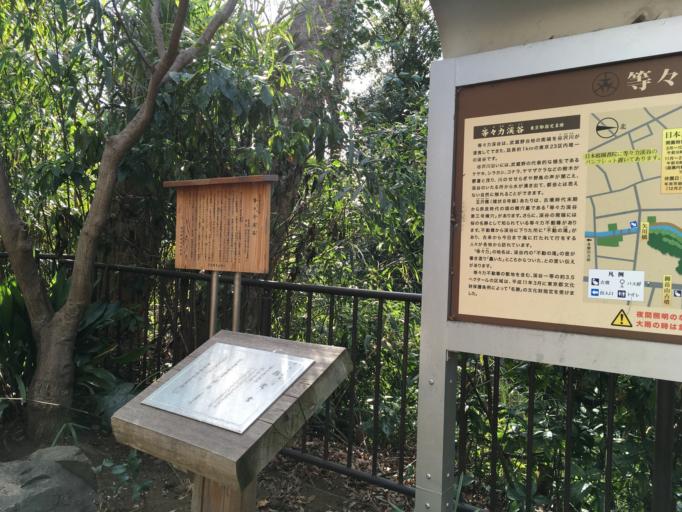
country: JP
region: Tokyo
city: Tokyo
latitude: 35.6078
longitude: 139.6467
